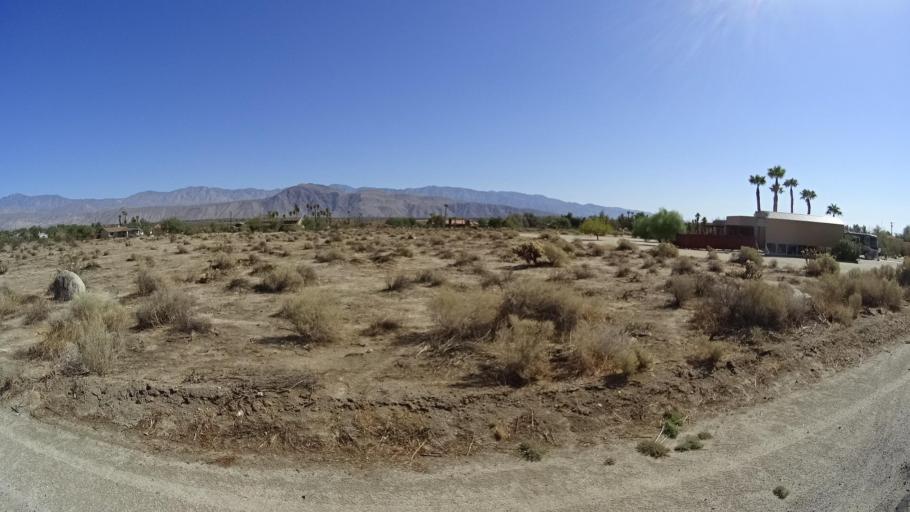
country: US
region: California
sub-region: San Diego County
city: Borrego Springs
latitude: 33.2724
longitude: -116.3868
